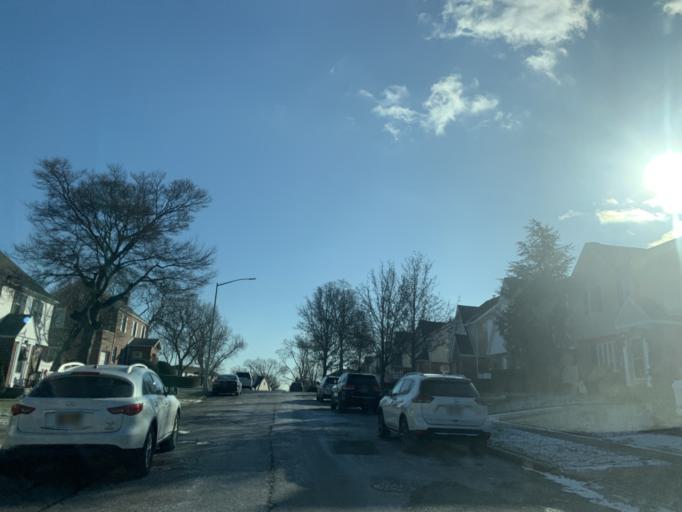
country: US
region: New York
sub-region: Nassau County
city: East Atlantic Beach
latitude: 40.7858
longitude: -73.8200
